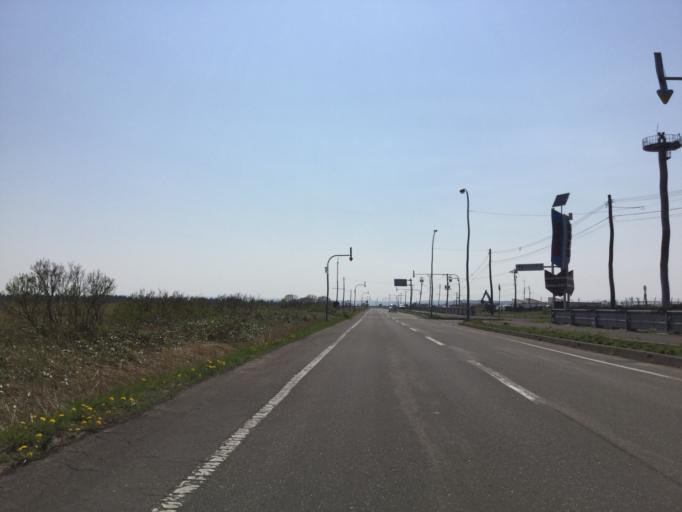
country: JP
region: Hokkaido
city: Makubetsu
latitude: 45.3983
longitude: 141.7981
